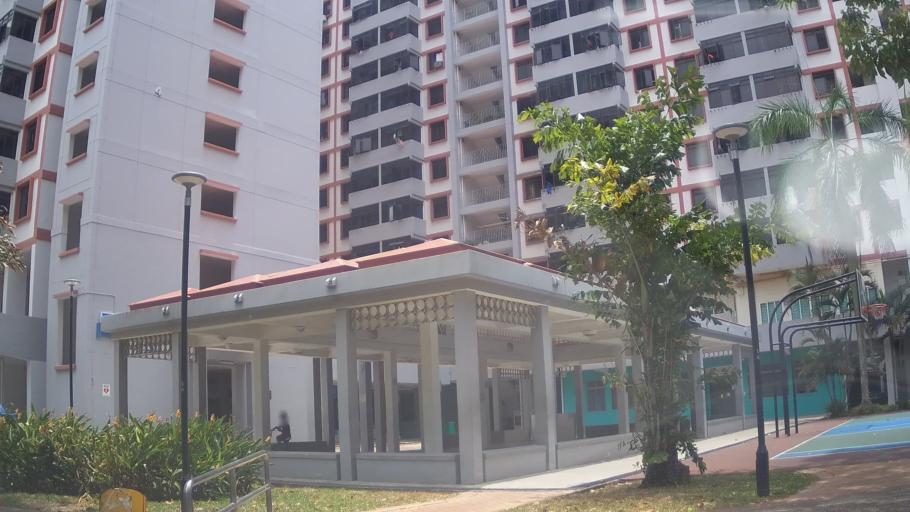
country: SG
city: Singapore
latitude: 1.3048
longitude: 103.8646
